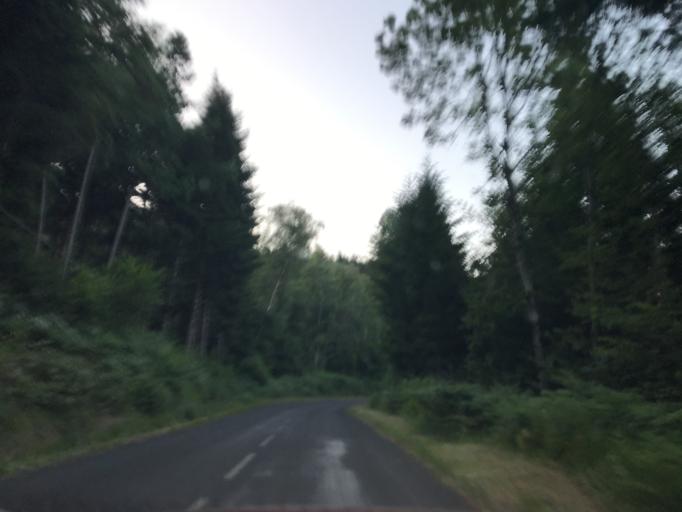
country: FR
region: Auvergne
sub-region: Departement du Puy-de-Dome
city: Celles-sur-Durolle
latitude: 45.7508
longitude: 3.6550
